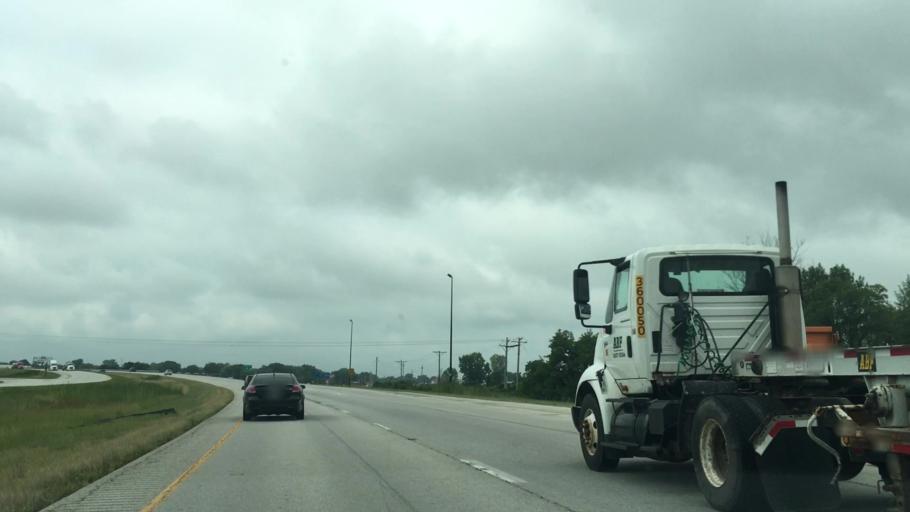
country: US
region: Illinois
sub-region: Rock Island County
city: Milan
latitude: 41.4558
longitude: -90.5428
